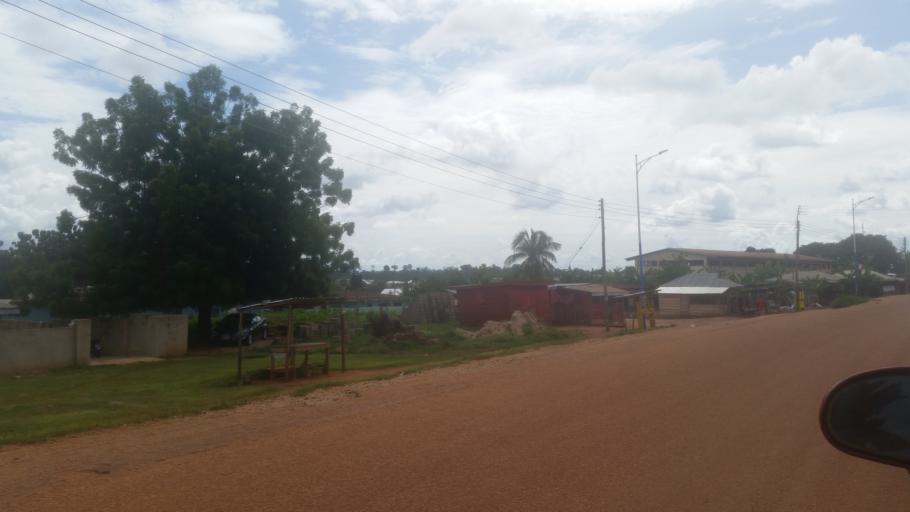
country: GH
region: Western
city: Bibiani
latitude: 6.8049
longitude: -2.5223
